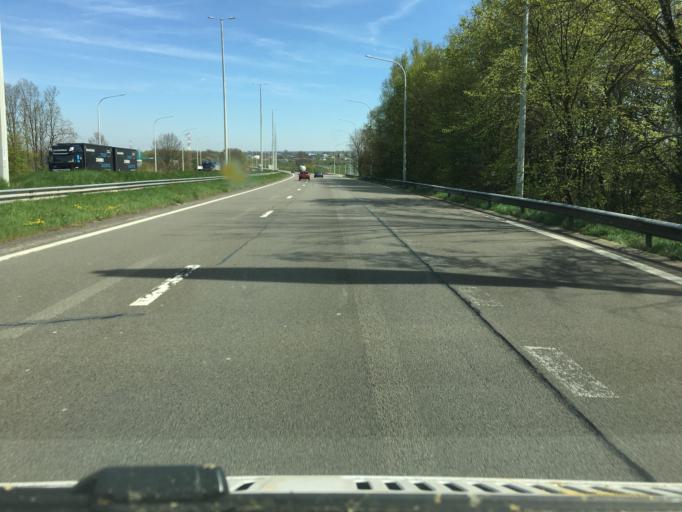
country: BE
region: Wallonia
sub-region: Province de Liege
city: Baelen
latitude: 50.6466
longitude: 5.9802
